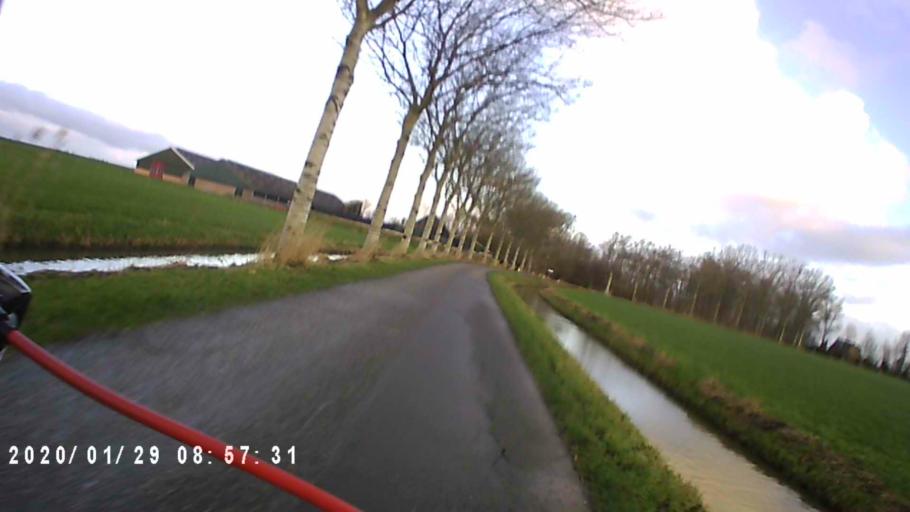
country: NL
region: Groningen
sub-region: Gemeente Zuidhorn
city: Aduard
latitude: 53.3164
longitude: 6.4546
